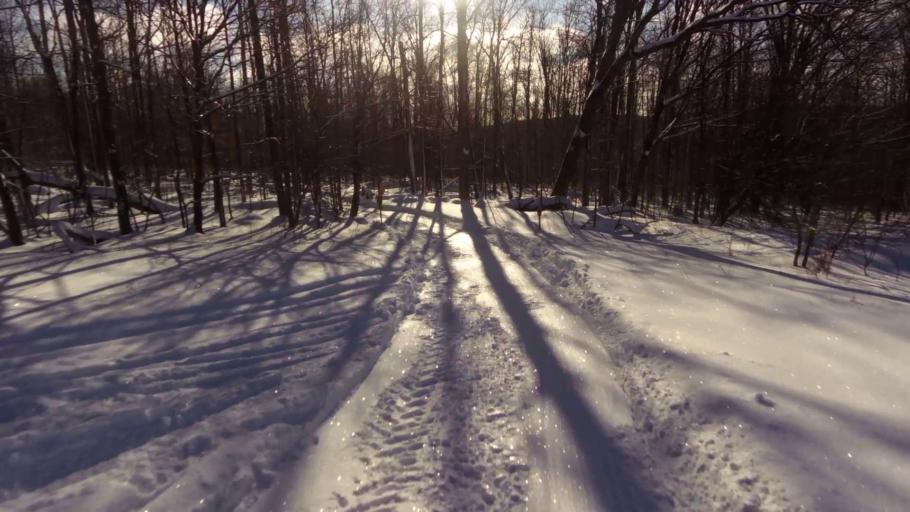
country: US
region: New York
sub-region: Chautauqua County
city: Falconer
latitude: 42.2599
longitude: -79.1734
